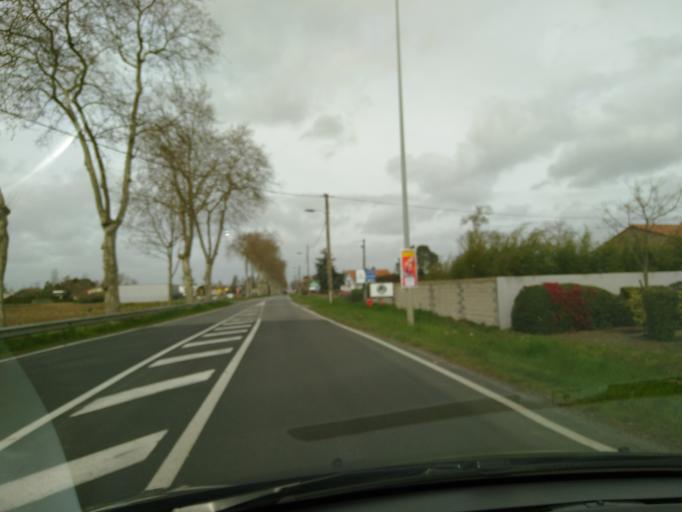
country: FR
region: Midi-Pyrenees
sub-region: Departement de la Haute-Garonne
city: Grenade
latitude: 43.7570
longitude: 1.3020
